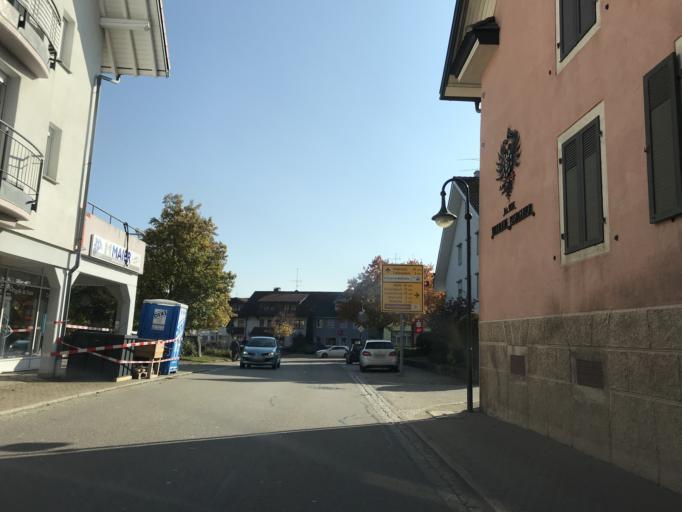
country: DE
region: Baden-Wuerttemberg
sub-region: Freiburg Region
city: Gorwihl
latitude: 47.6418
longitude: 8.0782
